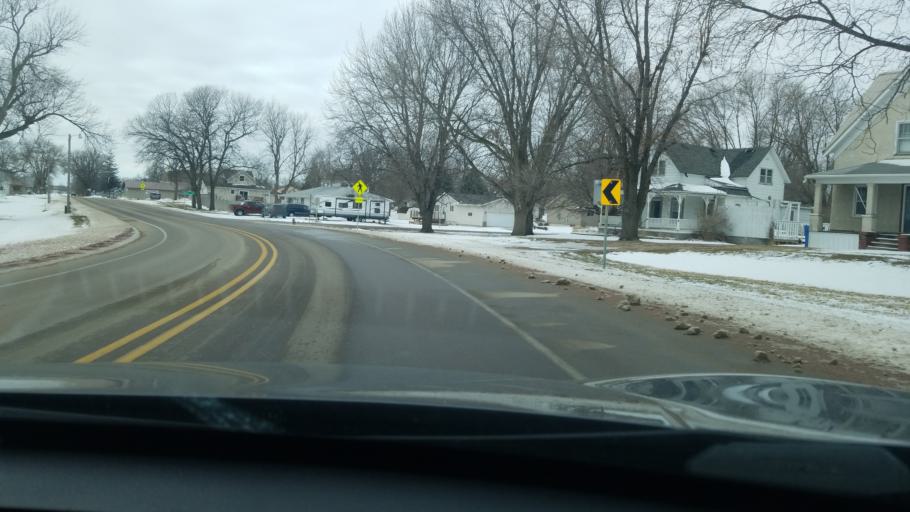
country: US
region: South Dakota
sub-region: Minnehaha County
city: Brandon
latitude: 43.4529
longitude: -96.4305
